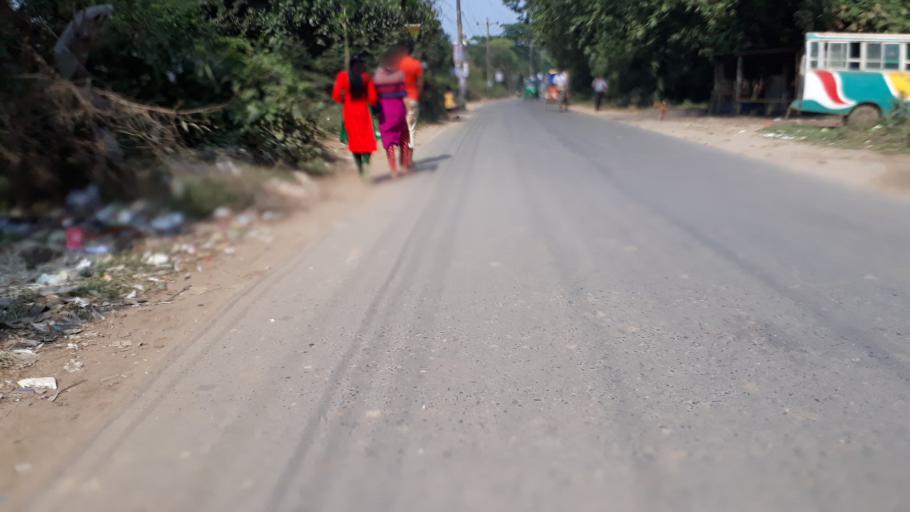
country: BD
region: Dhaka
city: Tungi
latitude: 23.8585
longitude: 90.3110
